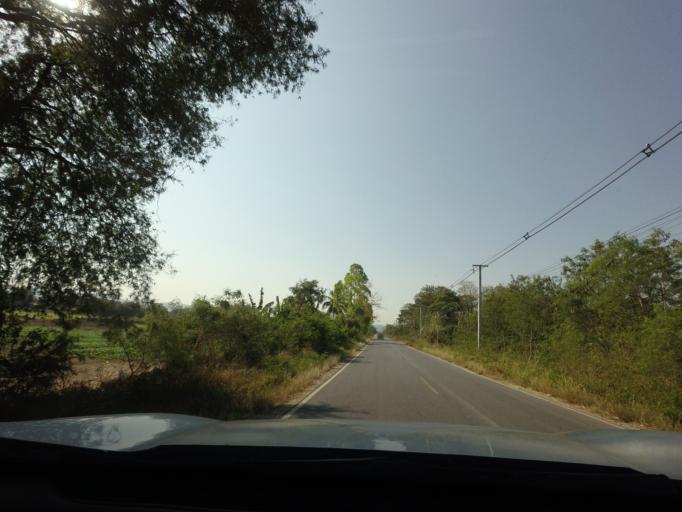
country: TH
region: Nakhon Ratchasima
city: Pak Chong
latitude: 14.6197
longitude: 101.4842
